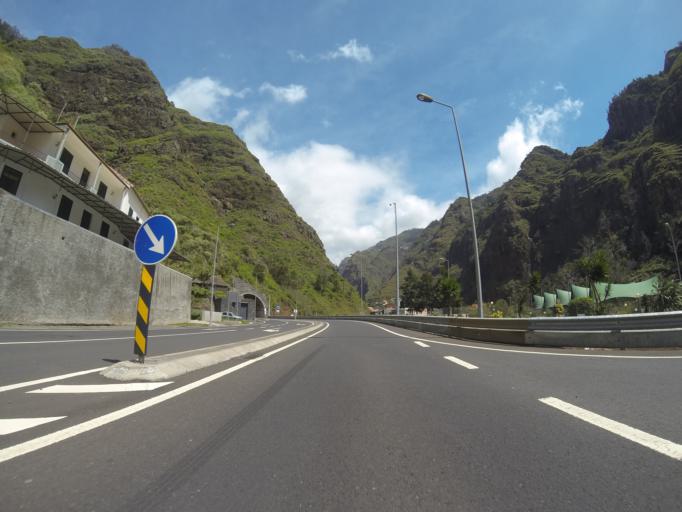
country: PT
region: Madeira
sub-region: Ribeira Brava
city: Campanario
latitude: 32.6915
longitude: -17.0486
